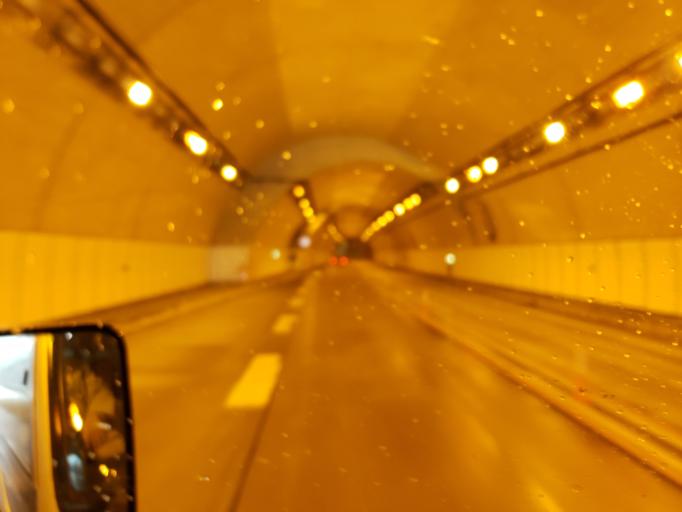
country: JP
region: Hyogo
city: Toyooka
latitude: 35.2311
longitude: 134.7835
